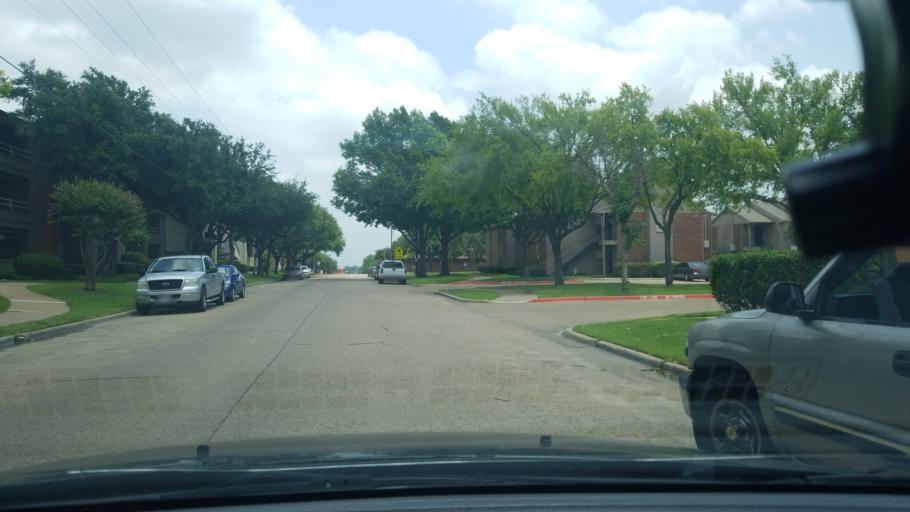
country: US
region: Texas
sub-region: Dallas County
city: Mesquite
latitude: 32.8051
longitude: -96.6173
